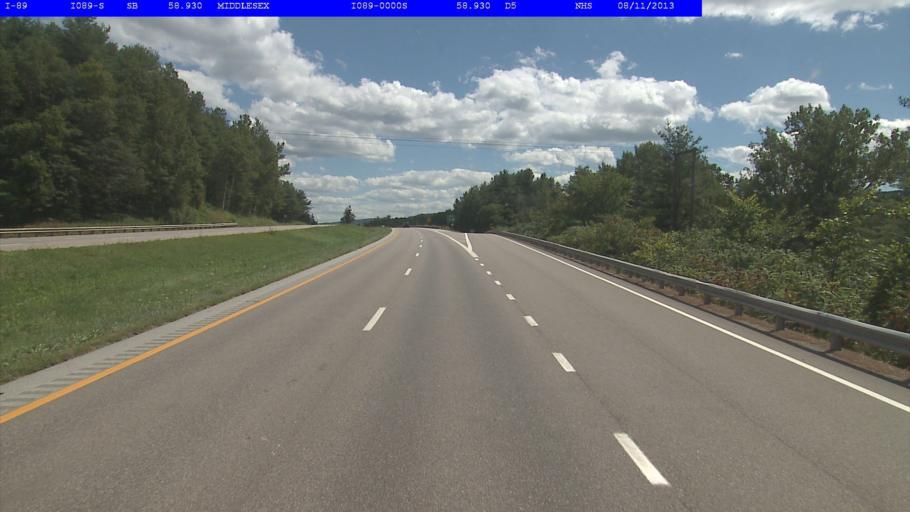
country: US
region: Vermont
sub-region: Washington County
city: Waterbury
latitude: 44.3006
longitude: -72.6882
